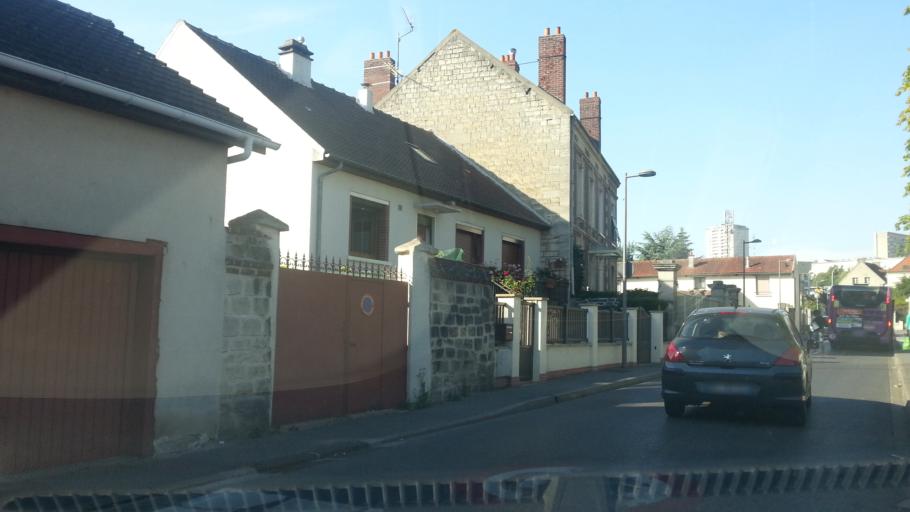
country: FR
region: Picardie
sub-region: Departement de l'Oise
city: Montataire
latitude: 49.2573
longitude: 2.4308
